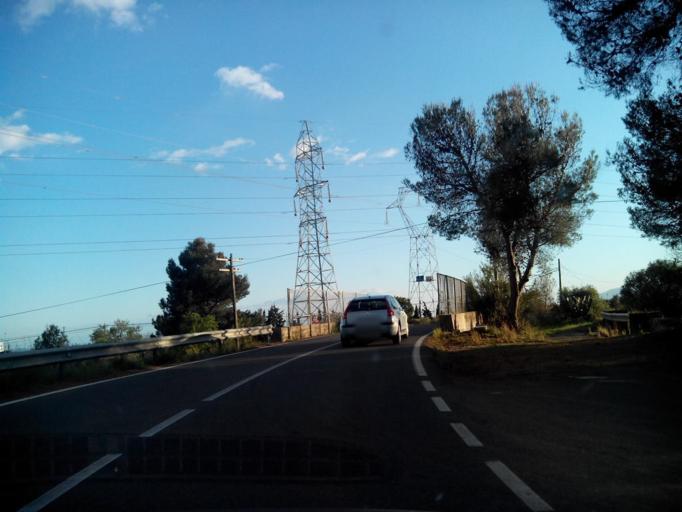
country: ES
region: Catalonia
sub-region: Provincia de Tarragona
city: Riudoms
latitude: 41.1673
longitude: 1.0593
